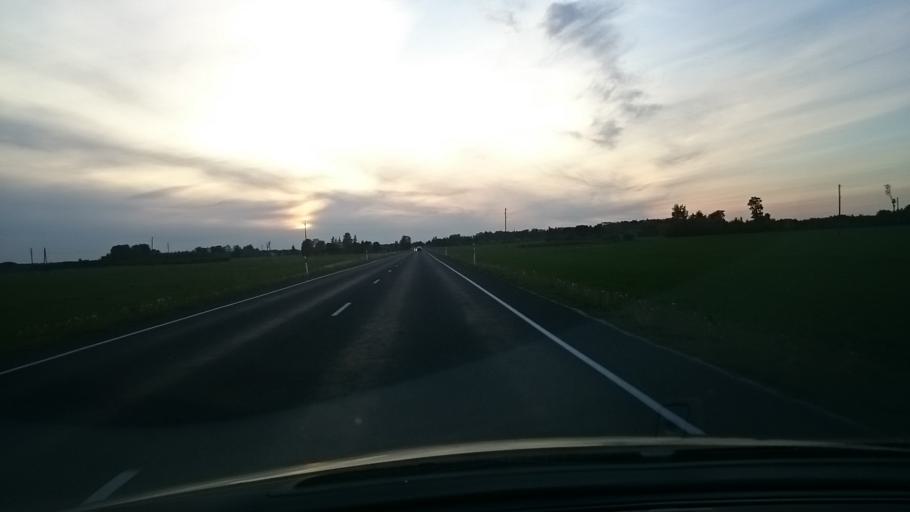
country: EE
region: Viljandimaa
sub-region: Vohma linn
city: Vohma
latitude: 58.7462
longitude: 25.5744
